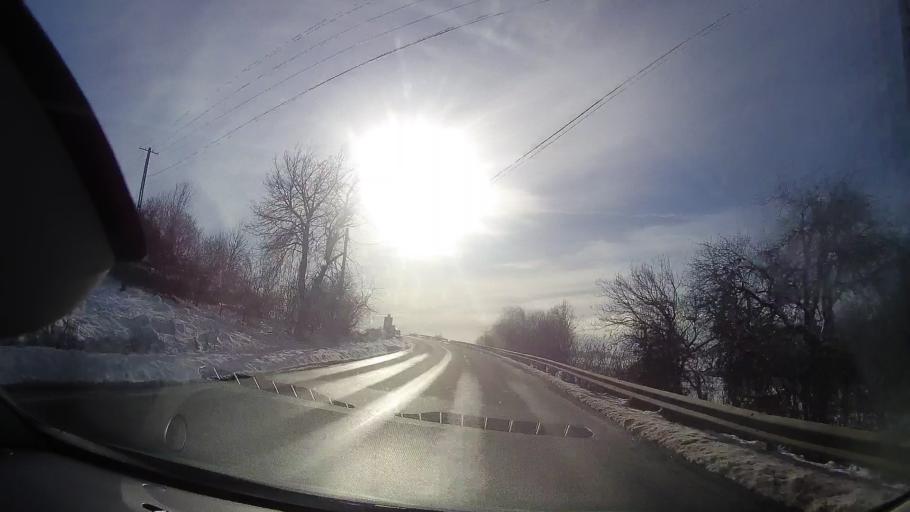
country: RO
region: Neamt
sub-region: Comuna Baltatesti
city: Valea Seaca
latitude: 47.1647
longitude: 26.3185
